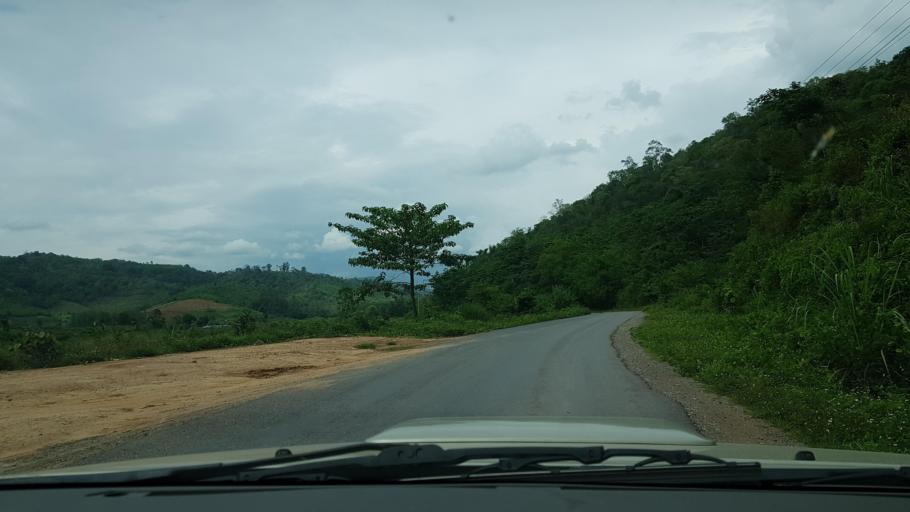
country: LA
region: Loungnamtha
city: Muang Nale
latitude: 20.4001
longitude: 101.7567
